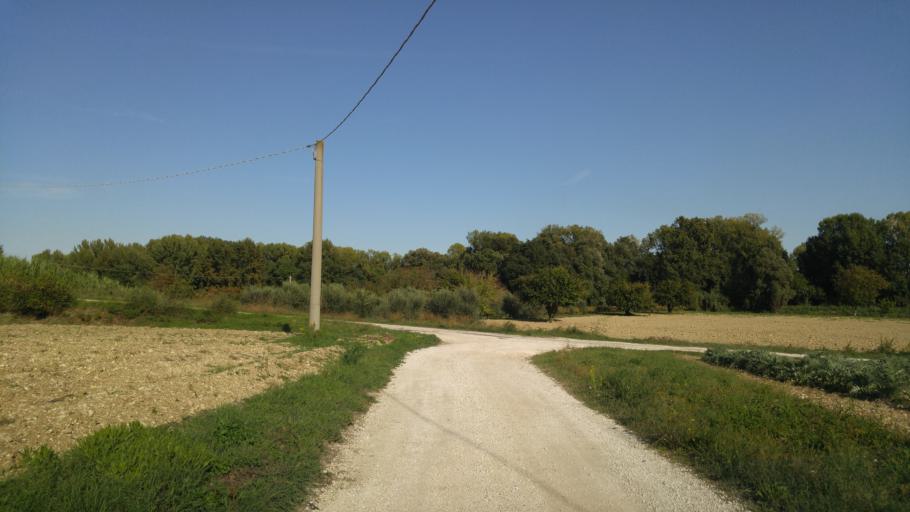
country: IT
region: The Marches
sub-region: Provincia di Pesaro e Urbino
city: Bellocchi
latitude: 43.7933
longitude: 13.0219
